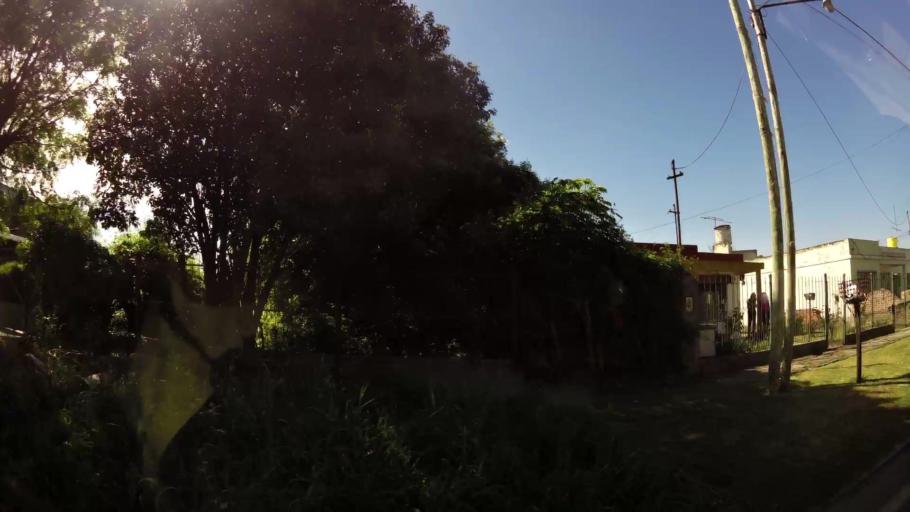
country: AR
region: Buenos Aires
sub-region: Partido de Almirante Brown
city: Adrogue
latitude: -34.8016
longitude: -58.3582
